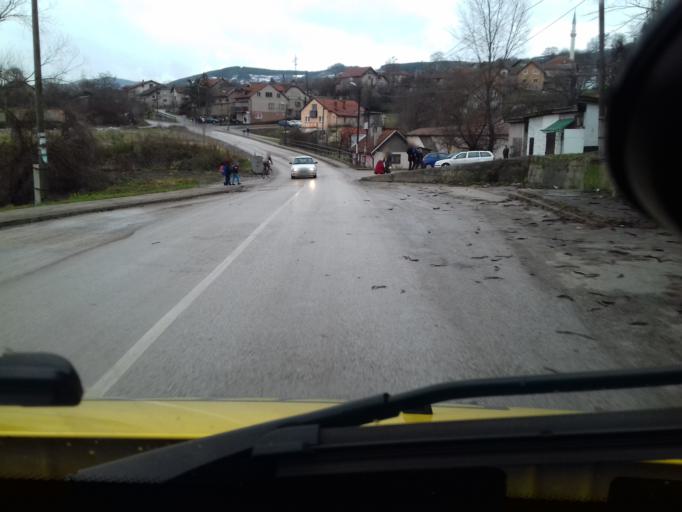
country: BA
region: Federation of Bosnia and Herzegovina
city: Zenica
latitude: 44.2320
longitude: 17.8888
